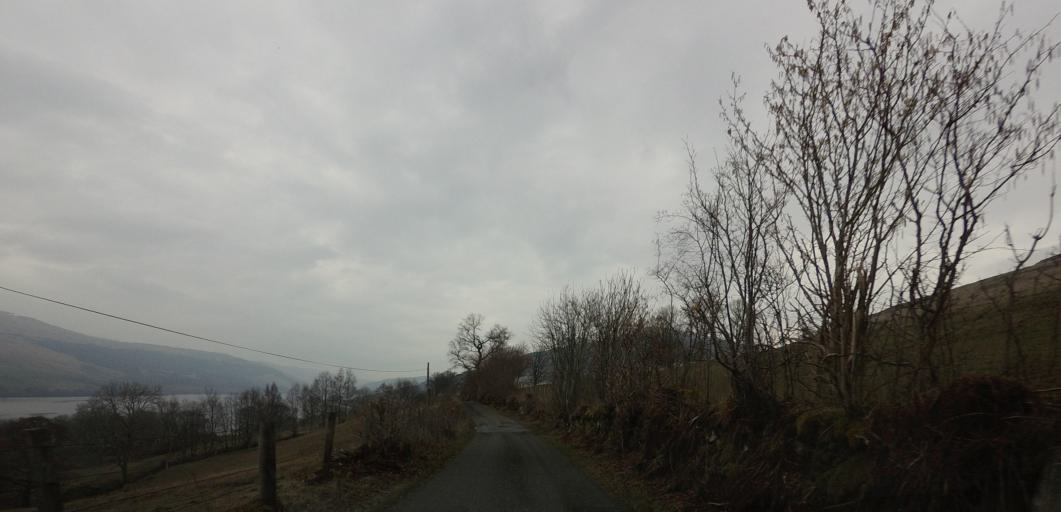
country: GB
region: Scotland
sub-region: Perth and Kinross
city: Comrie
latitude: 56.5197
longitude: -4.1216
